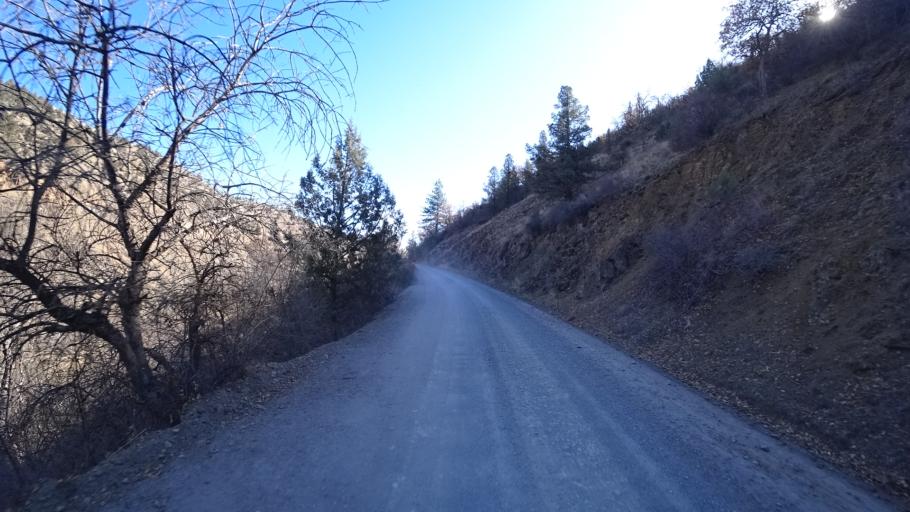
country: US
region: California
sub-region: Siskiyou County
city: Yreka
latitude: 41.7912
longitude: -122.6103
